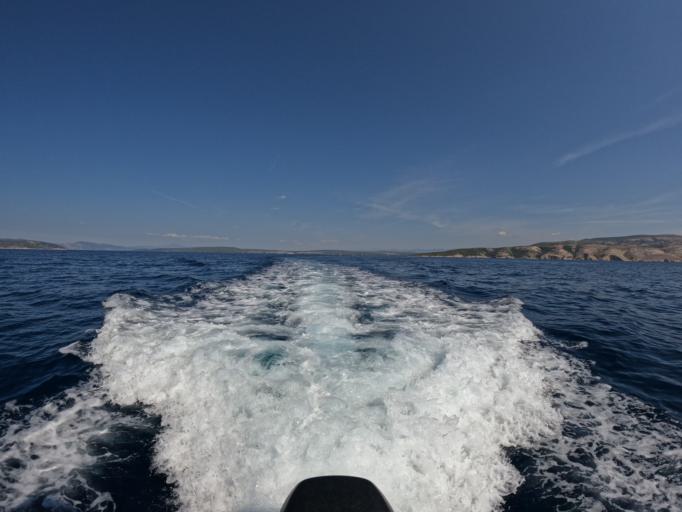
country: HR
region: Primorsko-Goranska
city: Punat
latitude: 44.9497
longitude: 14.6140
